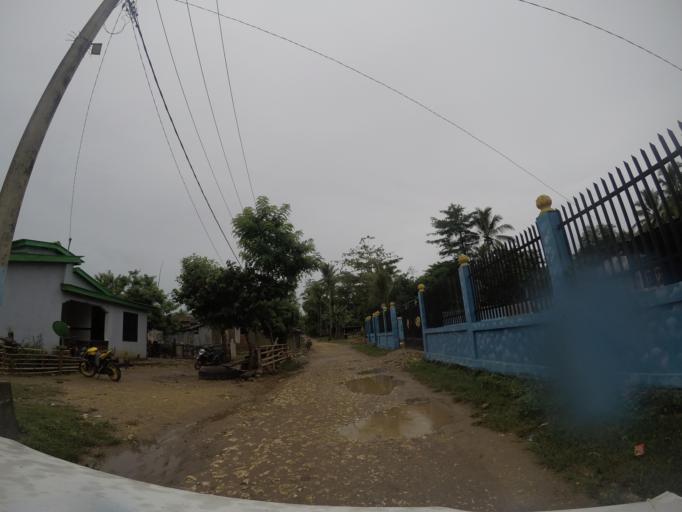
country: TL
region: Lautem
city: Lospalos
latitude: -8.5256
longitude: 127.0003
